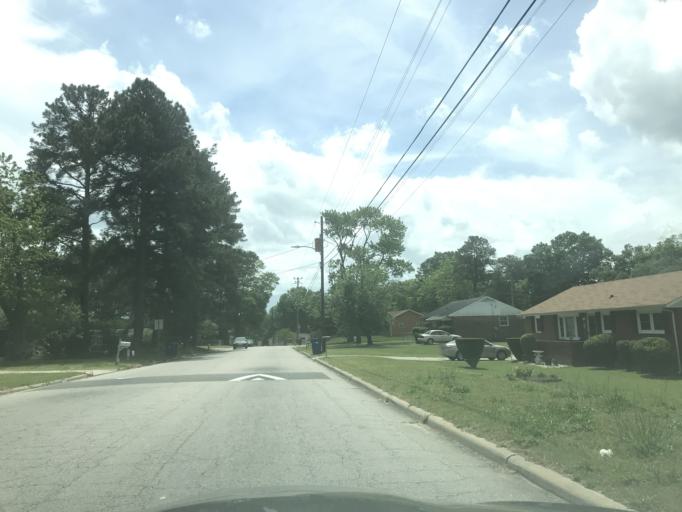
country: US
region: North Carolina
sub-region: Wake County
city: Raleigh
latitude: 35.7702
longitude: -78.5946
